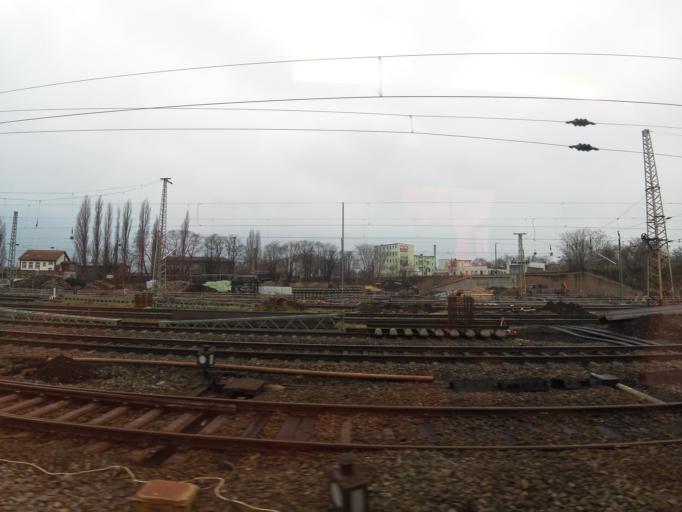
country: DE
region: Saxony-Anhalt
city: Halle (Saale)
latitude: 51.4891
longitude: 11.9894
